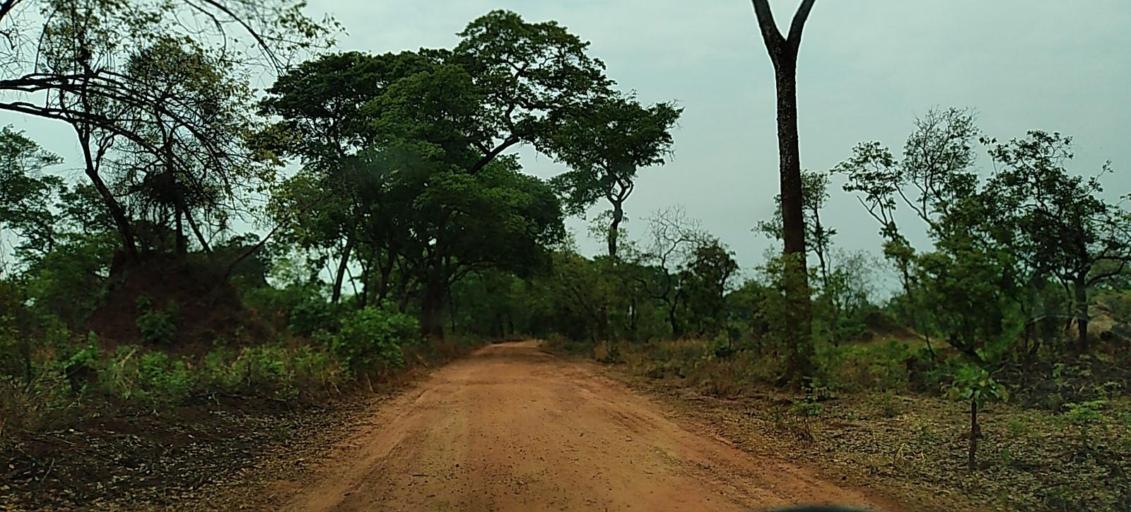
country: ZM
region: North-Western
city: Solwezi
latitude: -12.3316
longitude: 26.5216
